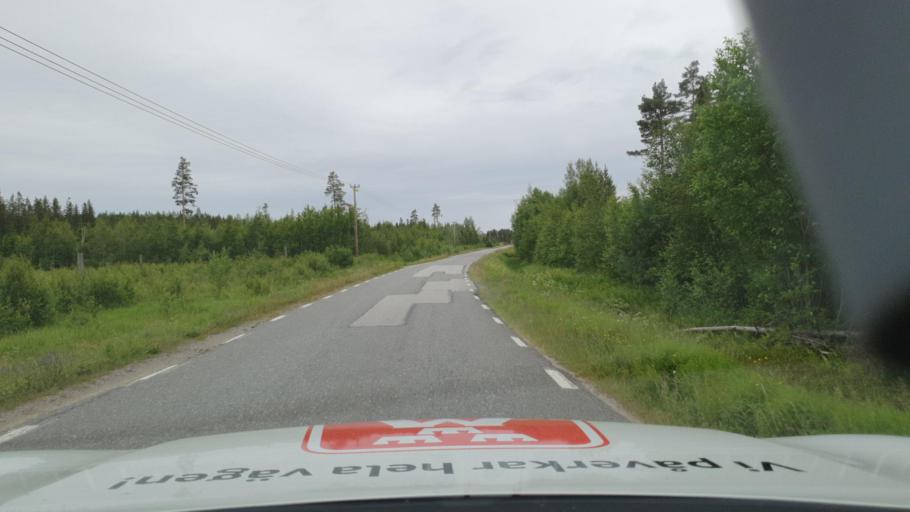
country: SE
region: Vaesterbotten
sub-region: Nordmalings Kommun
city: Nordmaling
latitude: 63.5184
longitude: 19.4213
